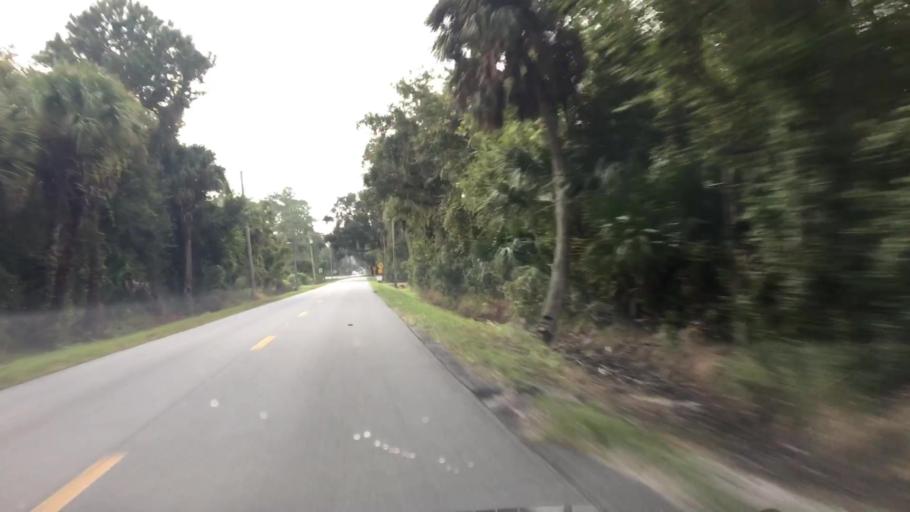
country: US
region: Florida
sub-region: Seminole County
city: Midway
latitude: 28.8496
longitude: -81.2044
